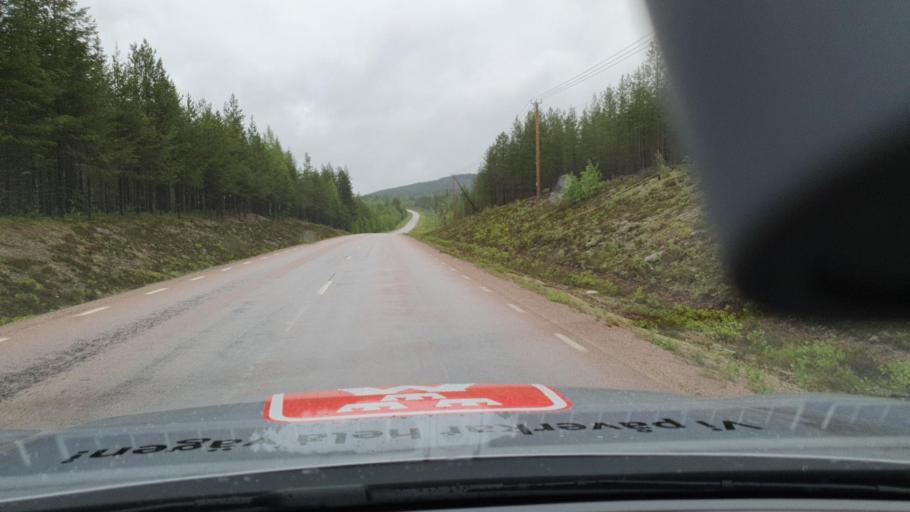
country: SE
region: Norrbotten
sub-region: Overkalix Kommun
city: OEverkalix
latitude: 66.4083
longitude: 22.9563
